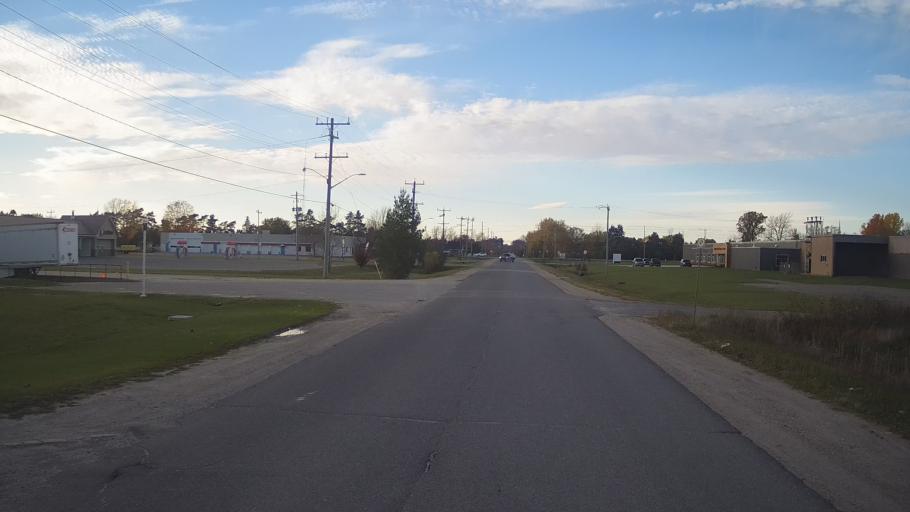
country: CA
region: Ontario
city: Perth
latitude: 44.8871
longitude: -76.2434
